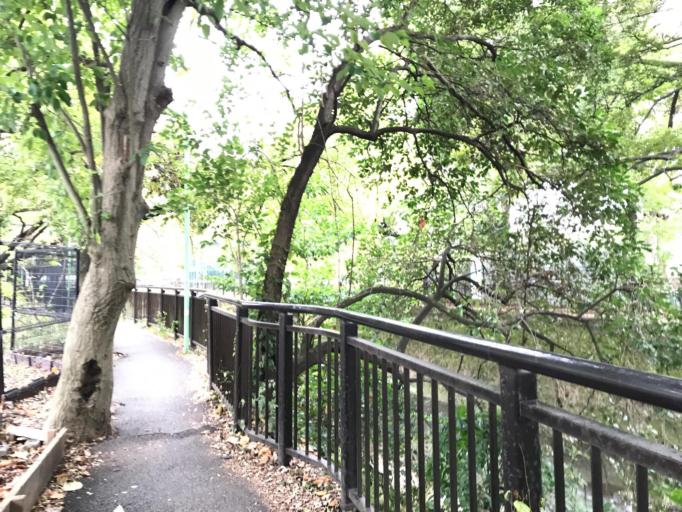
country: JP
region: Tokyo
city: Chofugaoka
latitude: 35.6456
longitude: 139.6020
